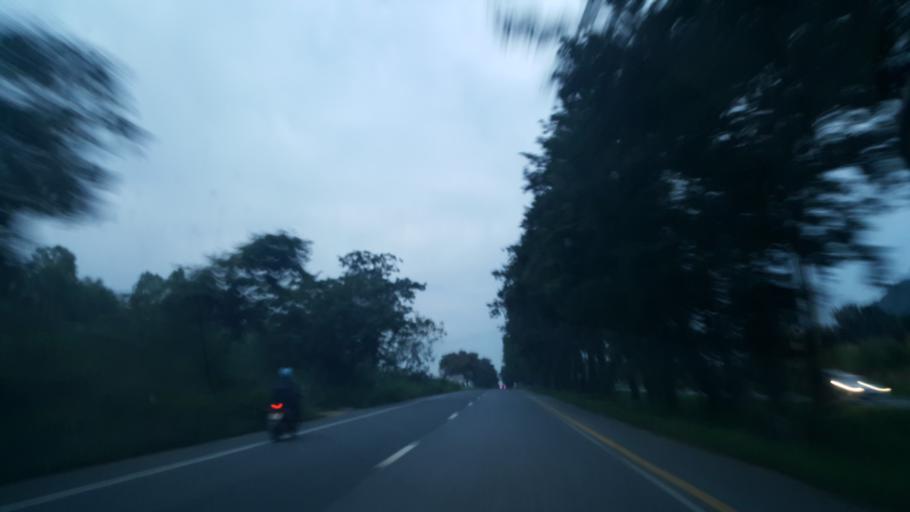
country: TH
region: Rayong
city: Ban Chang
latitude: 12.7788
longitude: 100.9919
